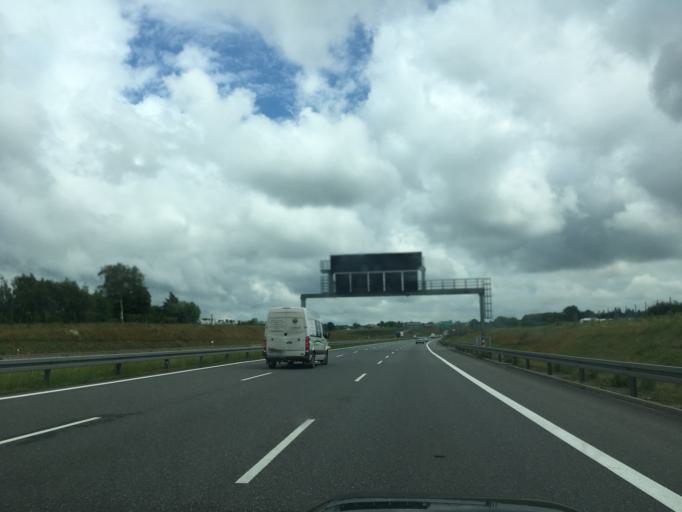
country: PL
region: Lublin Voivodeship
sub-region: Powiat lubelski
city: Jastkow
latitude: 51.3017
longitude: 22.4987
